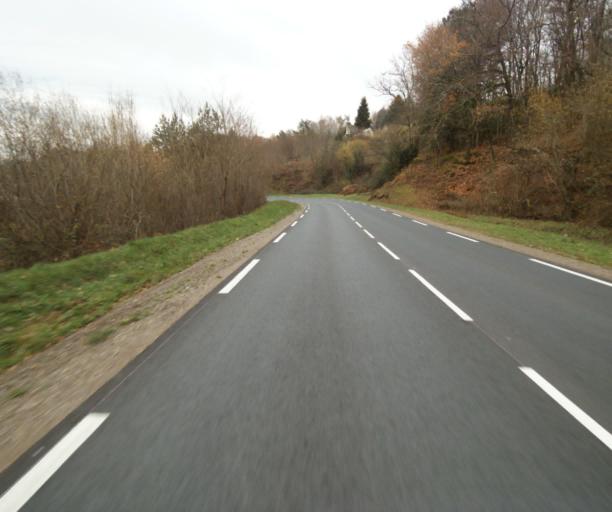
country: FR
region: Limousin
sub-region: Departement de la Correze
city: Tulle
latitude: 45.2665
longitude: 1.7336
